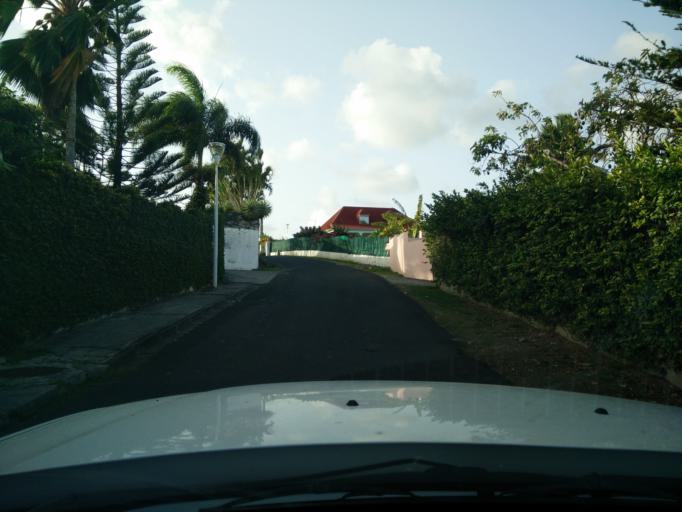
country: GP
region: Guadeloupe
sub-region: Guadeloupe
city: Le Gosier
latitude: 16.2015
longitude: -61.4717
